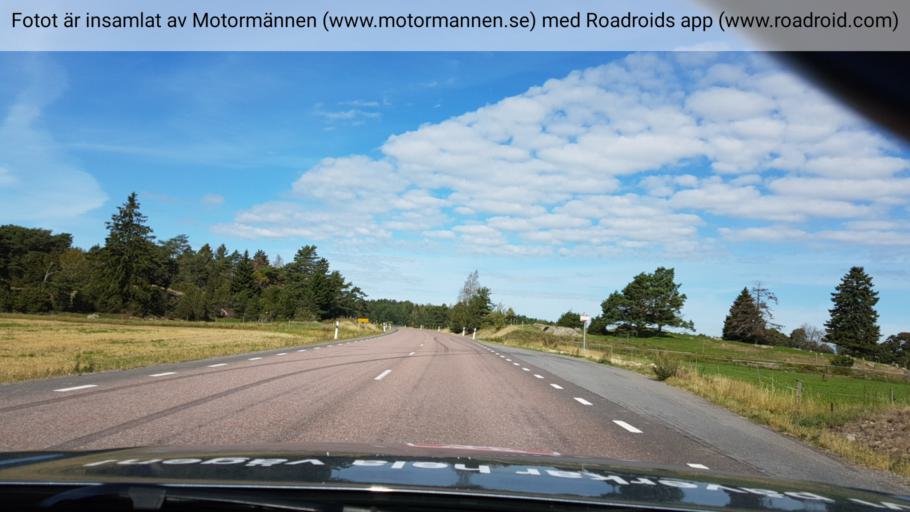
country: SE
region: Uppsala
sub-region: Osthammars Kommun
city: Bjorklinge
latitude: 59.9304
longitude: 17.4905
